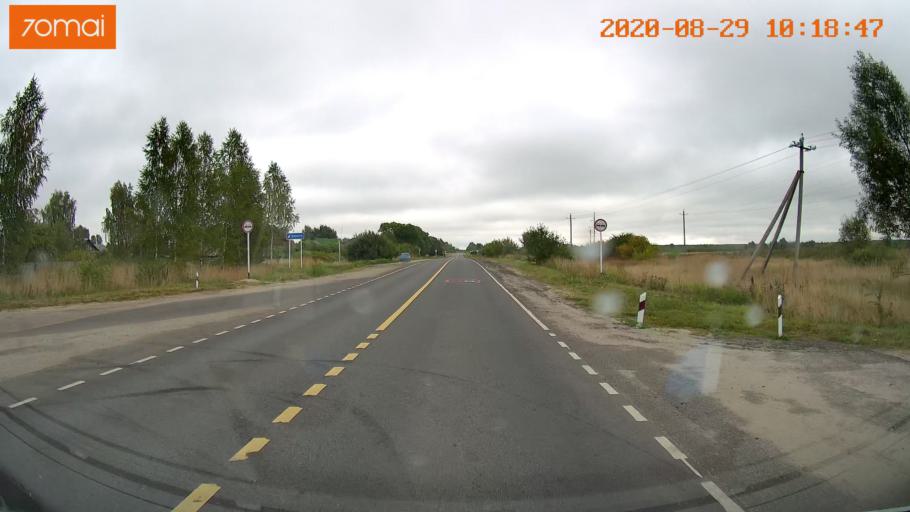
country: RU
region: Ivanovo
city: Yur'yevets
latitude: 57.3302
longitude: 42.8456
